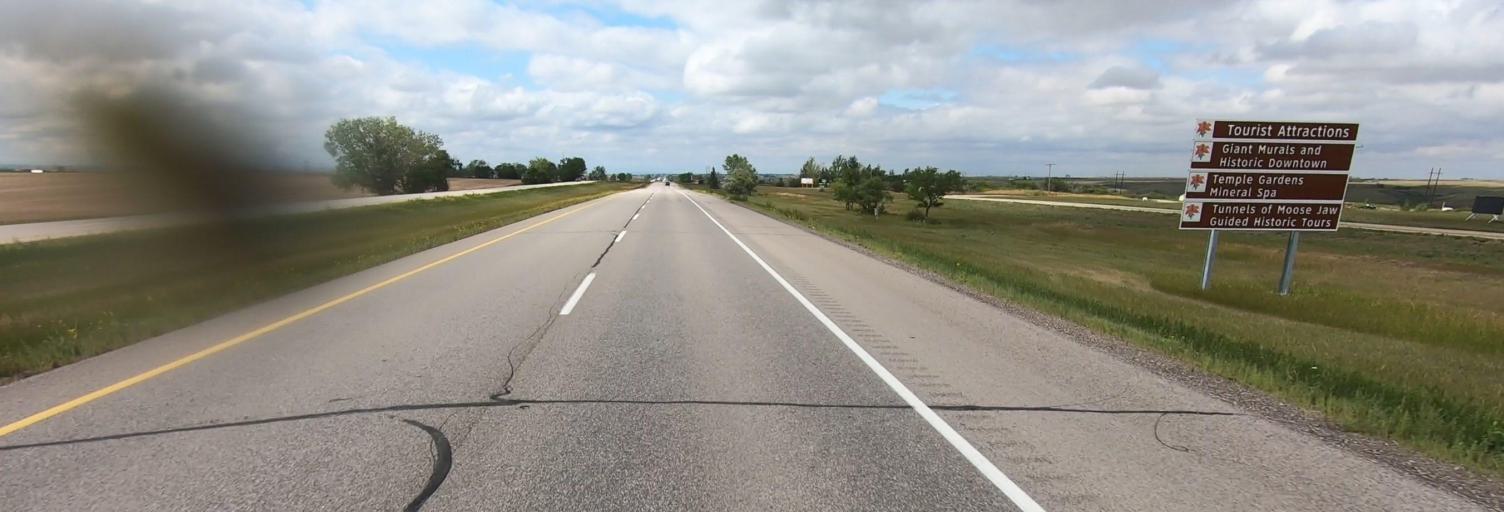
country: CA
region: Saskatchewan
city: Moose Jaw
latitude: 50.3973
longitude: -105.3548
